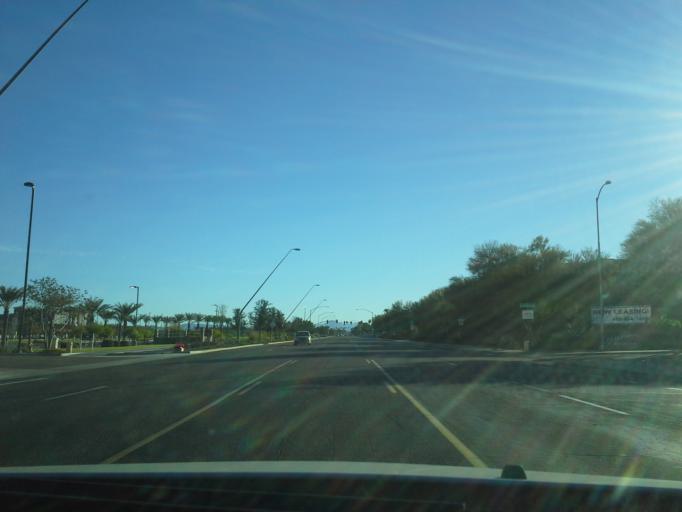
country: US
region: Arizona
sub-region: Maricopa County
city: Tempe
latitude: 33.4294
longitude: -111.8832
